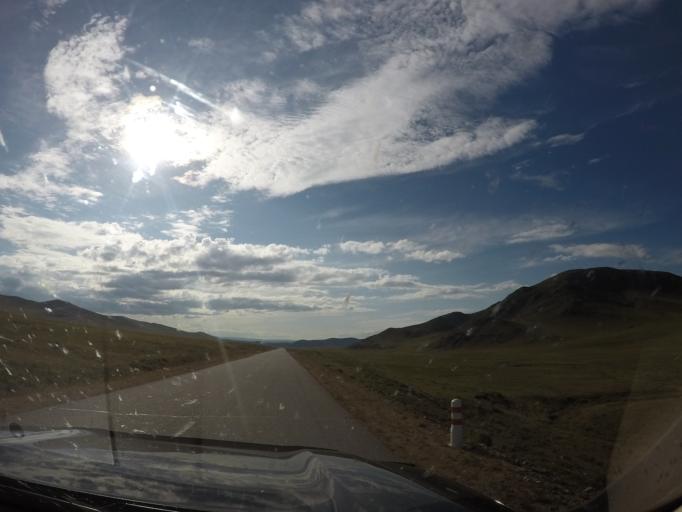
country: MN
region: Central Aimak
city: Bayandelger
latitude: 47.6933
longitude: 108.5358
